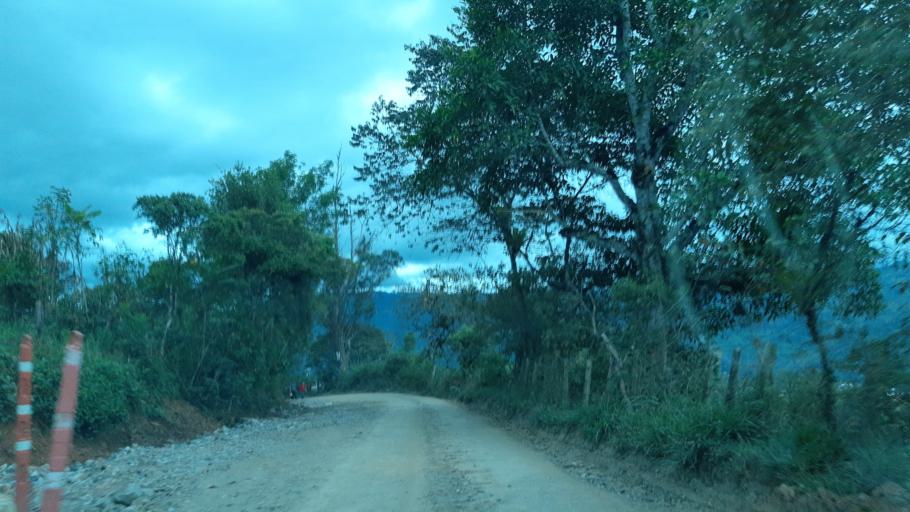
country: CO
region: Boyaca
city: Garagoa
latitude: 5.0850
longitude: -73.3592
